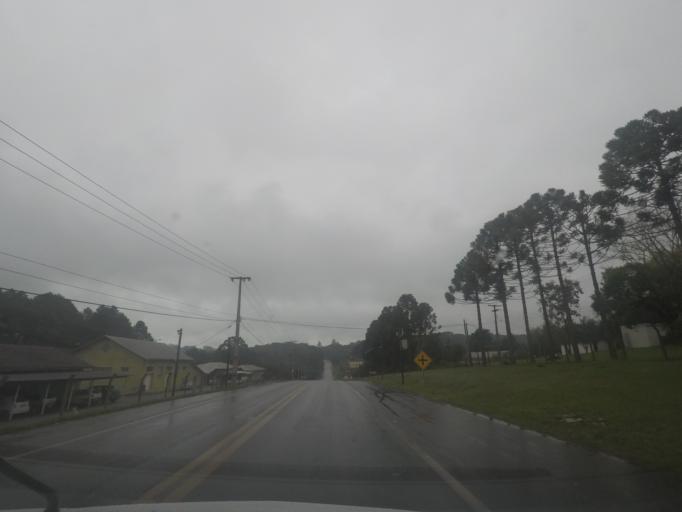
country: BR
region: Parana
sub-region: Colombo
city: Colombo
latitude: -25.3213
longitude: -49.1596
